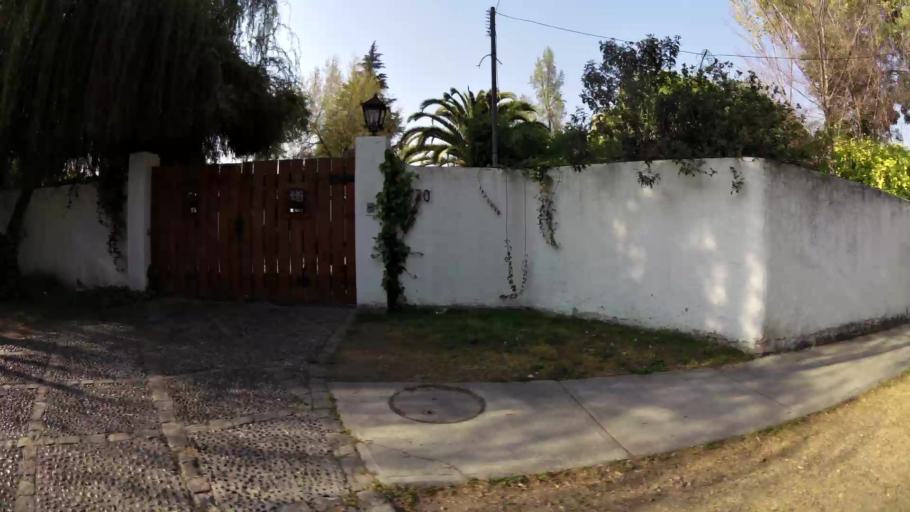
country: CL
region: Santiago Metropolitan
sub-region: Provincia de Santiago
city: Villa Presidente Frei, Nunoa, Santiago, Chile
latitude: -33.3666
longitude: -70.5258
